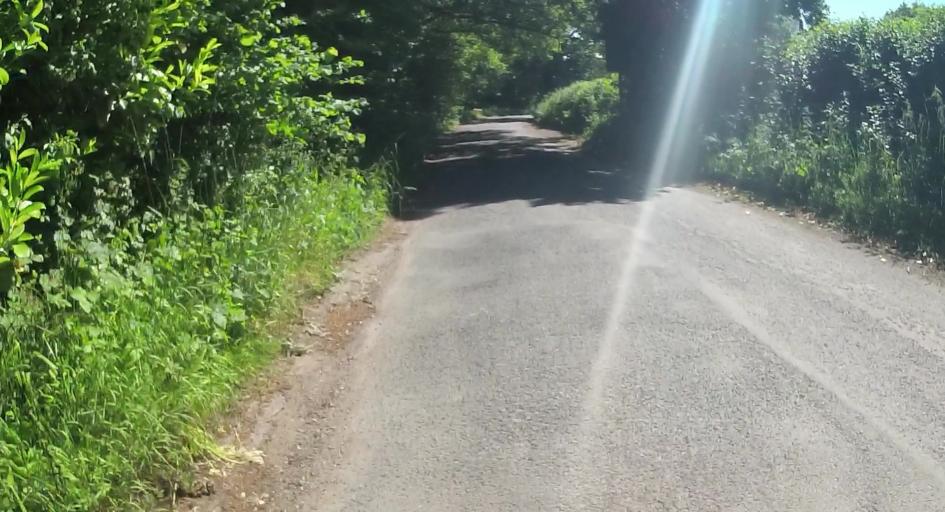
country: GB
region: England
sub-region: Hampshire
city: Hook
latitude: 51.2760
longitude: -0.9958
